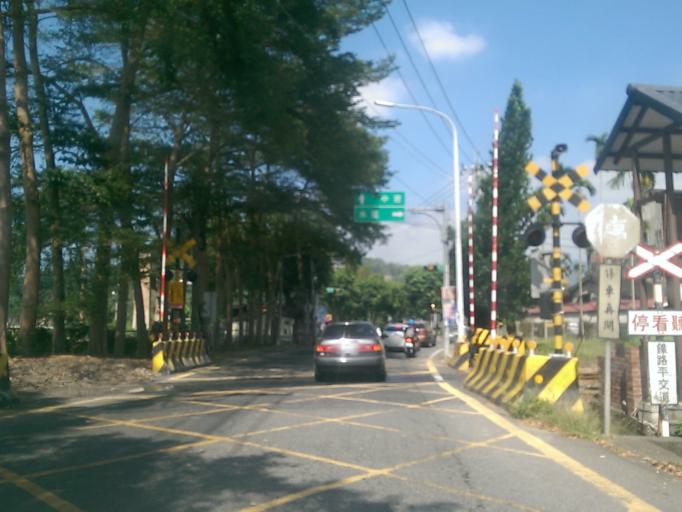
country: TW
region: Taiwan
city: Lugu
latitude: 23.8266
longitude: 120.7762
